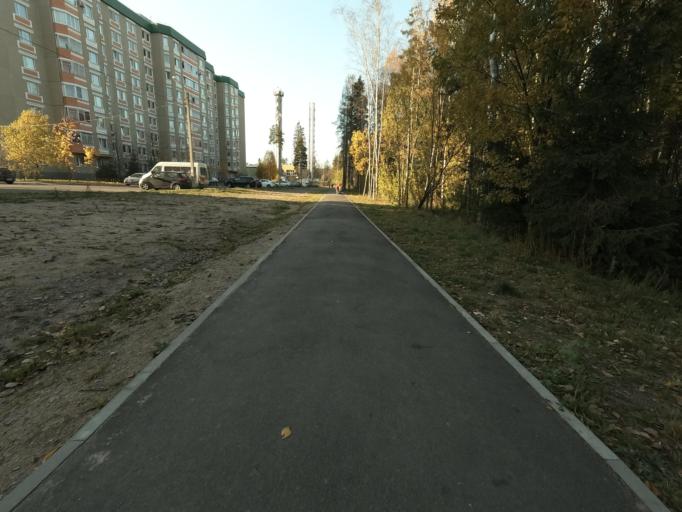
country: RU
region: Leningrad
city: Sertolovo
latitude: 60.1466
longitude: 30.2256
